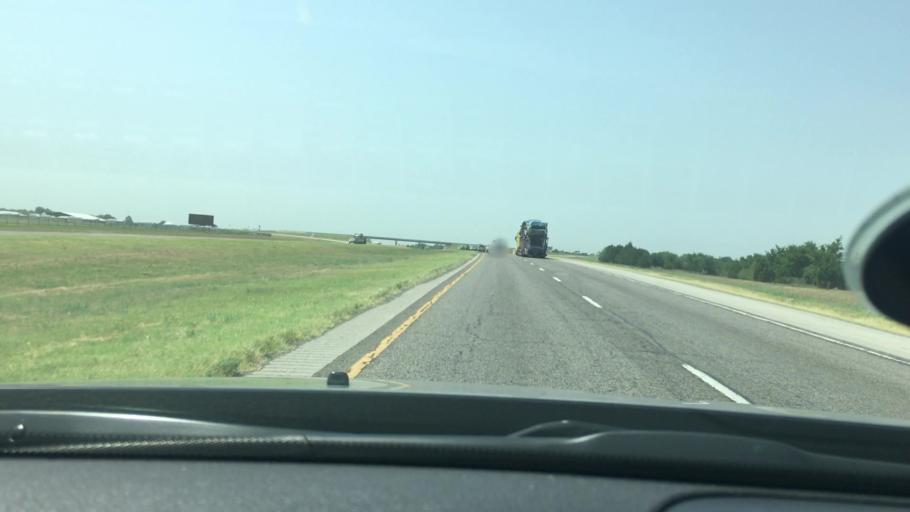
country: US
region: Oklahoma
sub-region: Garvin County
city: Wynnewood
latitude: 34.6293
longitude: -97.2173
